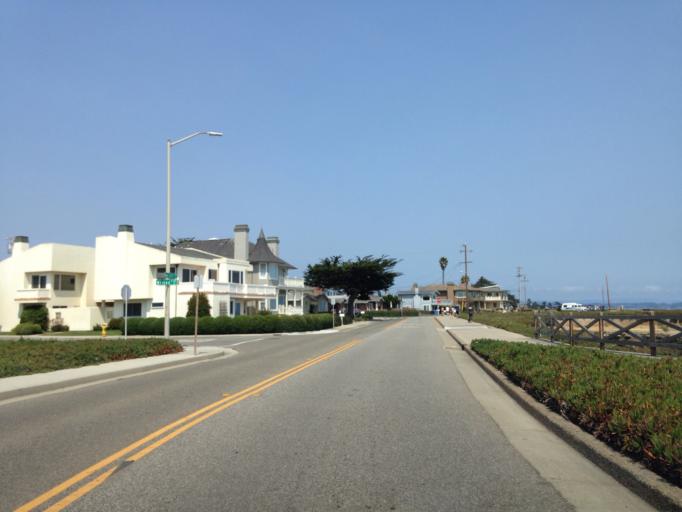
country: US
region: California
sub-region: Santa Cruz County
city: Santa Cruz
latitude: 36.9497
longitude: -122.0489
